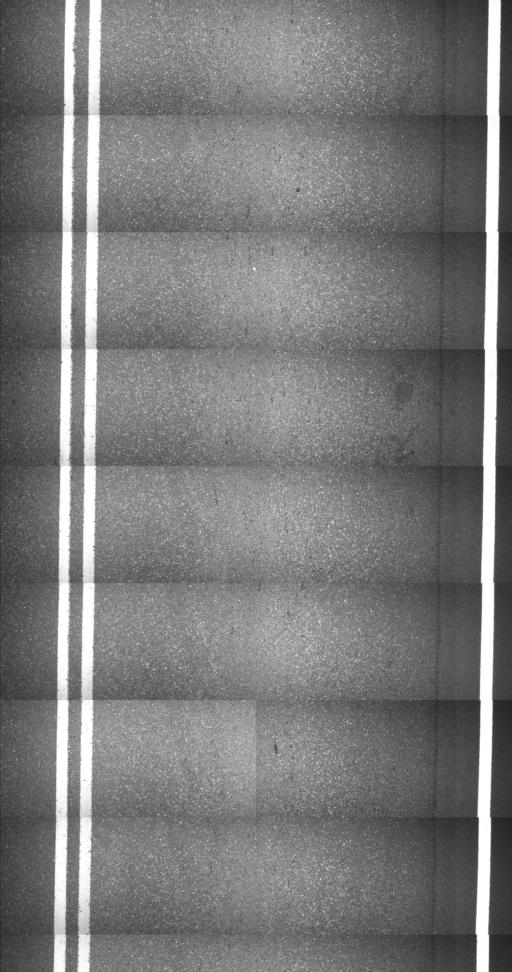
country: US
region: Vermont
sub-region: Orange County
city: Randolph
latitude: 43.9440
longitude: -72.6145
